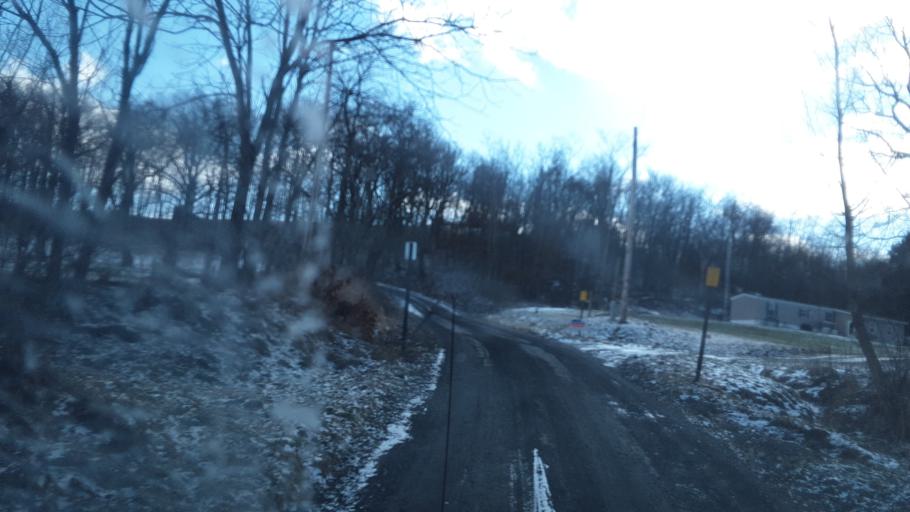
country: US
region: Ohio
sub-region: Carroll County
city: Carrollton
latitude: 40.5476
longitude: -81.0749
